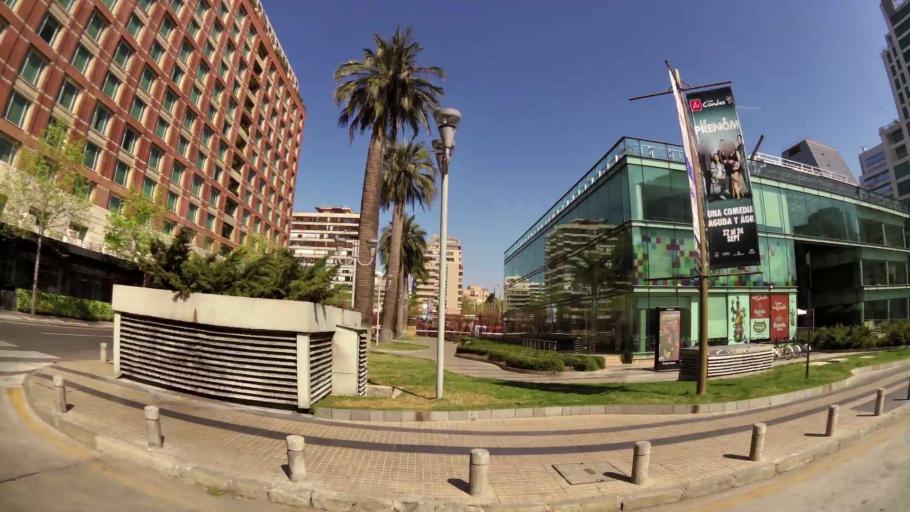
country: CL
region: Santiago Metropolitan
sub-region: Provincia de Santiago
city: Villa Presidente Frei, Nunoa, Santiago, Chile
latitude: -33.4156
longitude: -70.5957
